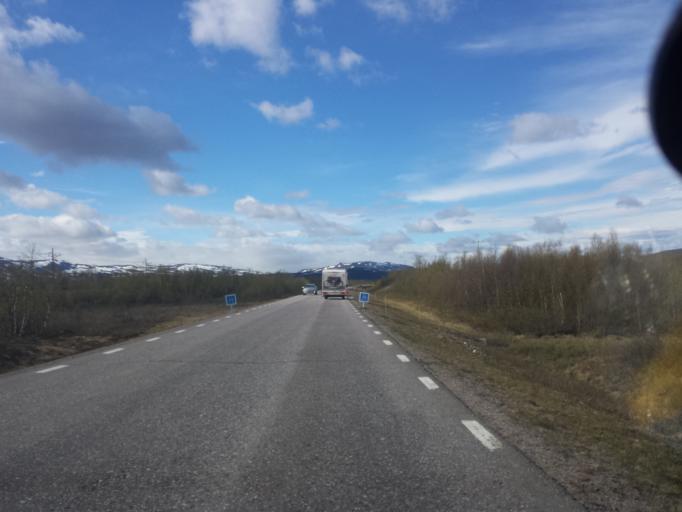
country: SE
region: Norrbotten
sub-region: Kiruna Kommun
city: Kiruna
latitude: 68.0046
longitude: 19.8527
